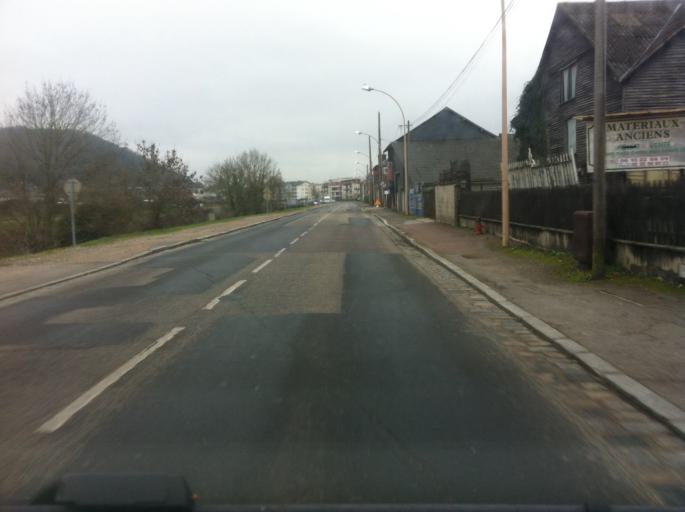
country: FR
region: Haute-Normandie
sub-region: Departement de l'Eure
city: Saint-Germain-Village
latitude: 49.3594
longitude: 0.5059
